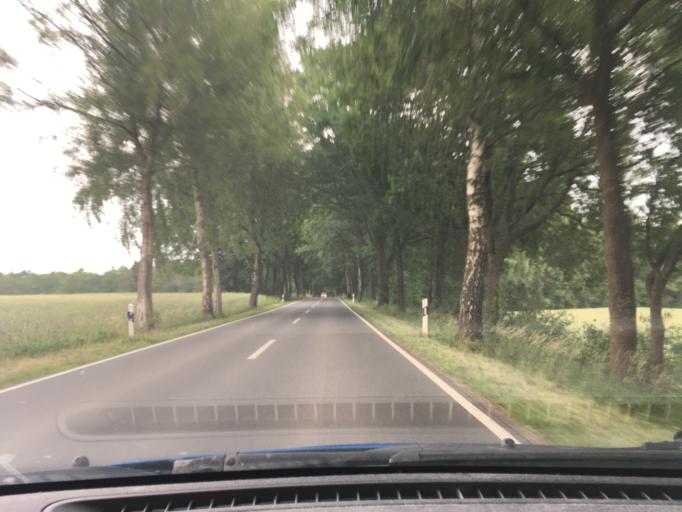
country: DE
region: Lower Saxony
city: Bad Fallingbostel
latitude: 52.8485
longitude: 9.6583
